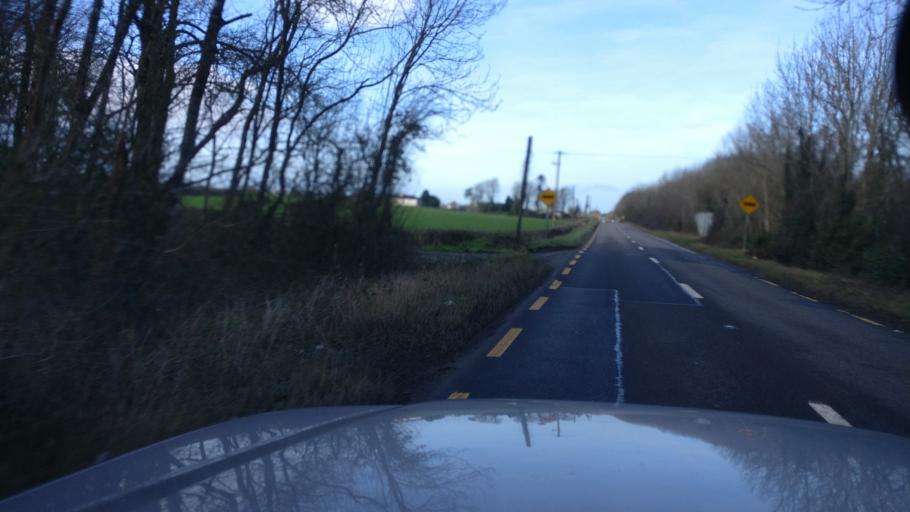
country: IE
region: Leinster
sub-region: Laois
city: Mountmellick
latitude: 53.0822
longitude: -7.3320
